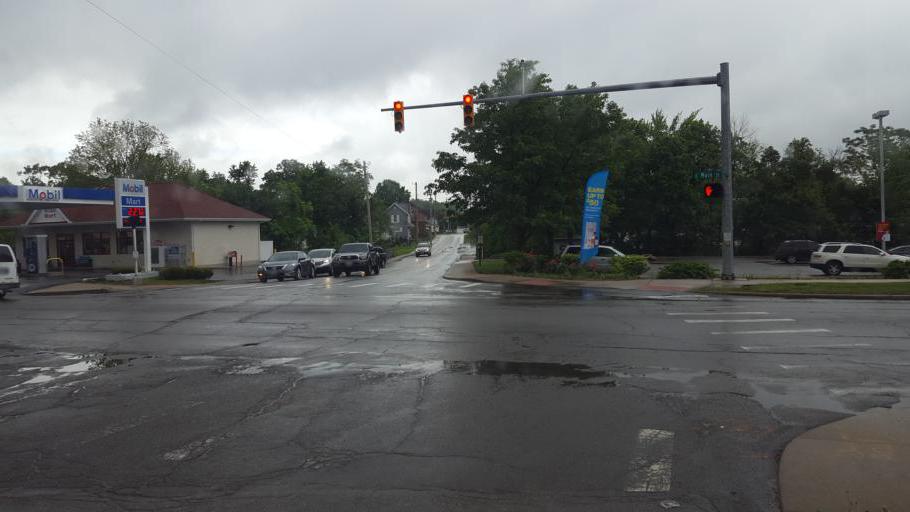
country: US
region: Ohio
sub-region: Ashland County
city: Ashland
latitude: 40.8679
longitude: -82.3077
